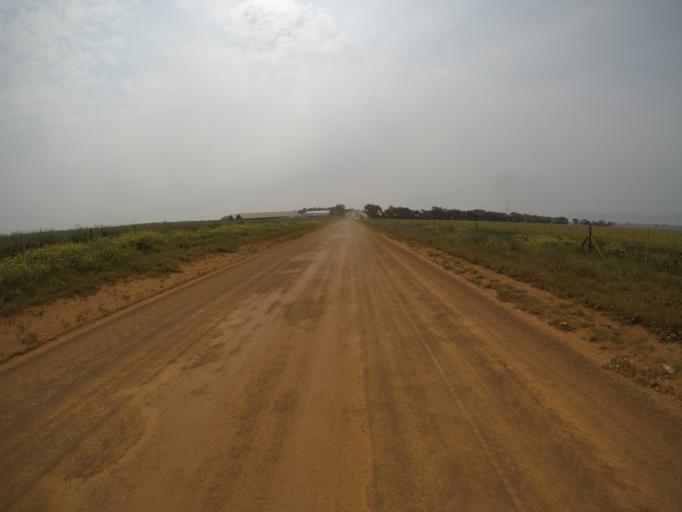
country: ZA
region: Western Cape
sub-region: City of Cape Town
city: Kraaifontein
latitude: -33.7083
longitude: 18.6895
